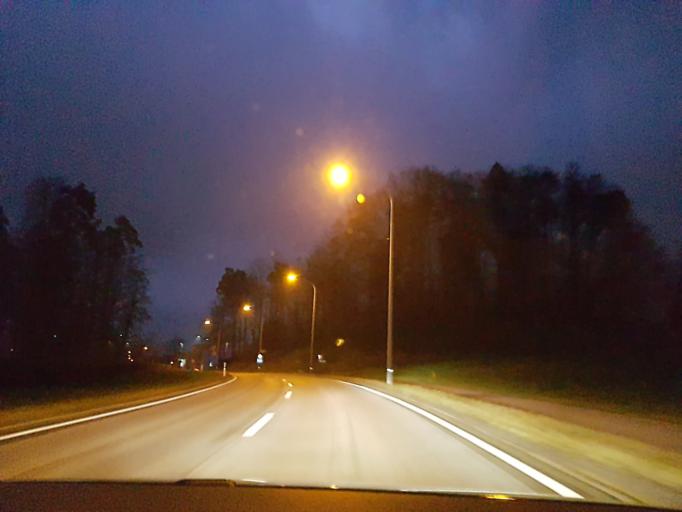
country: CH
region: Zurich
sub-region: Bezirk Horgen
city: Adliswil / Tal
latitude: 47.3073
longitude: 8.5393
